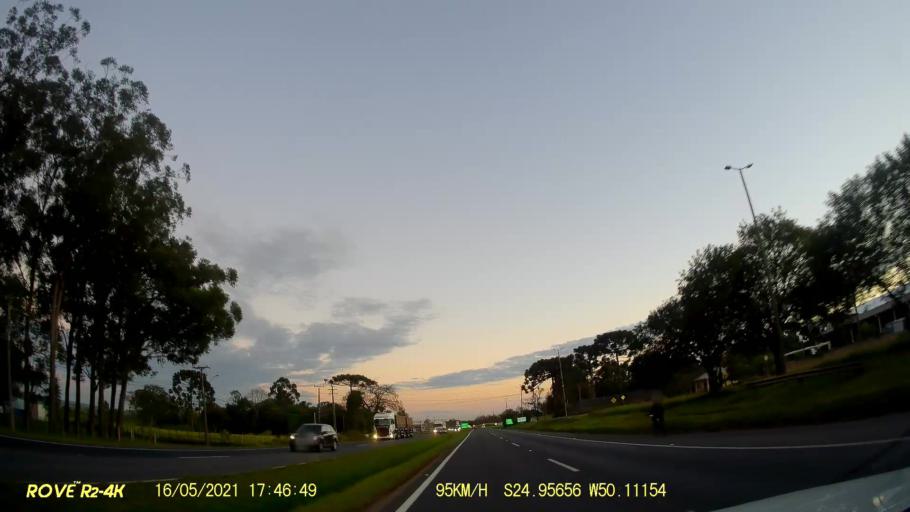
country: BR
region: Parana
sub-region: Carambei
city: Carambei
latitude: -24.9566
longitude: -50.1115
